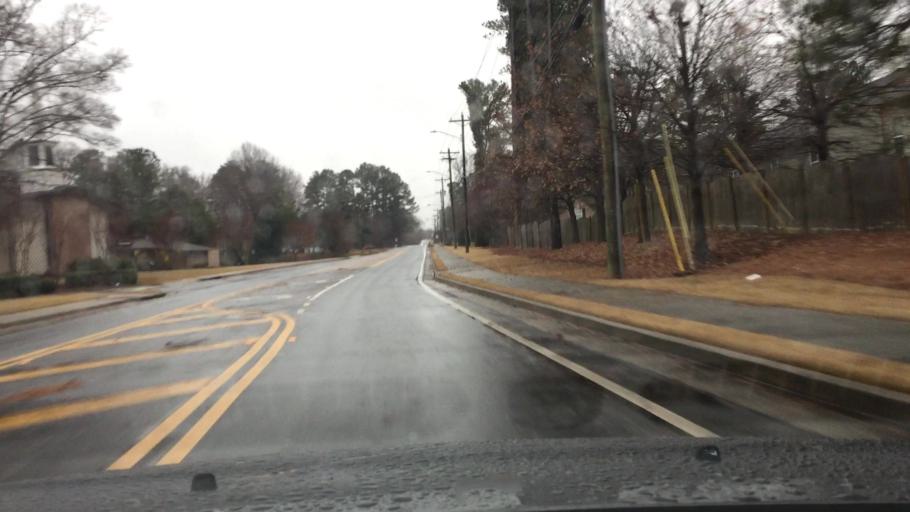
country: US
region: Georgia
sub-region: Cobb County
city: Fair Oaks
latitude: 33.9141
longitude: -84.5756
